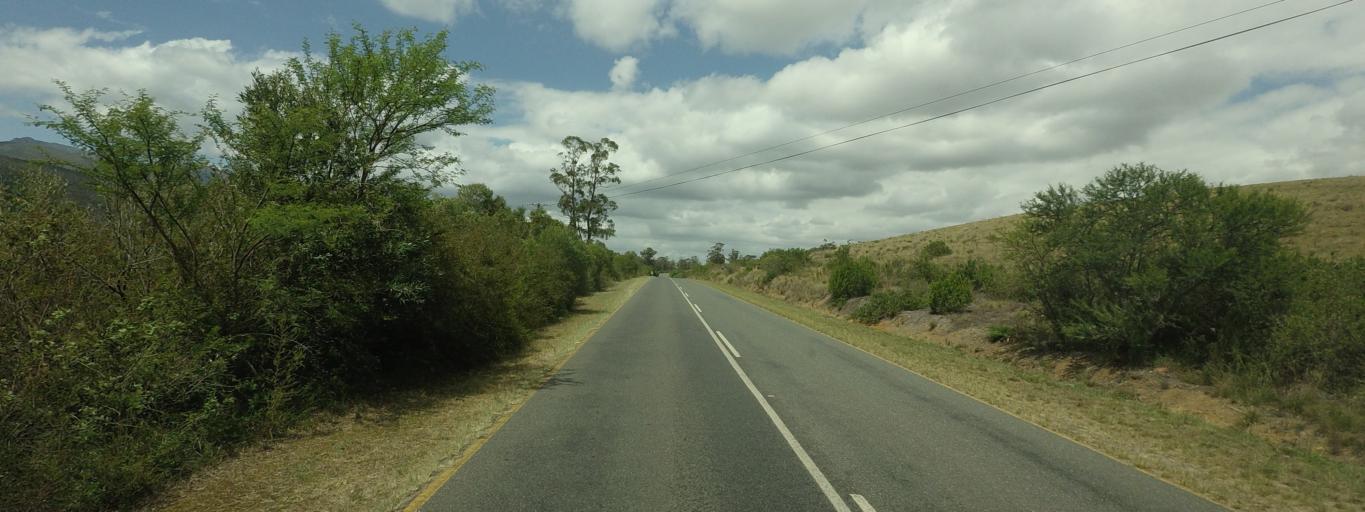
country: ZA
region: Western Cape
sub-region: Overberg District Municipality
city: Swellendam
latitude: -34.0050
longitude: 20.6784
